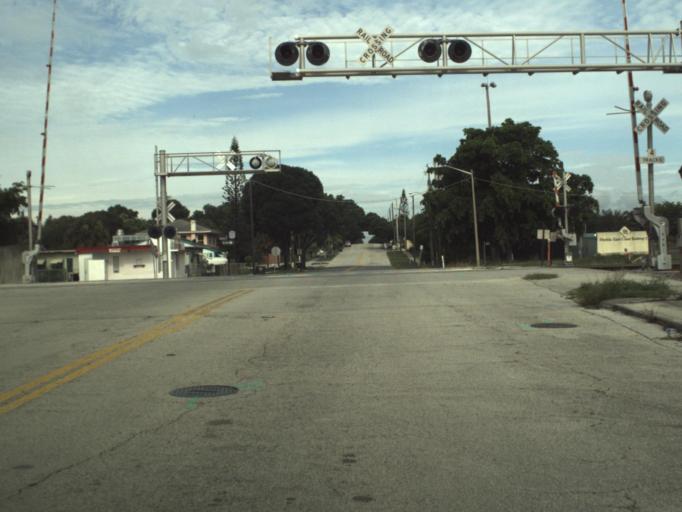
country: US
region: Florida
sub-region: Palm Beach County
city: West Palm Beach
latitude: 26.7273
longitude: -80.0566
